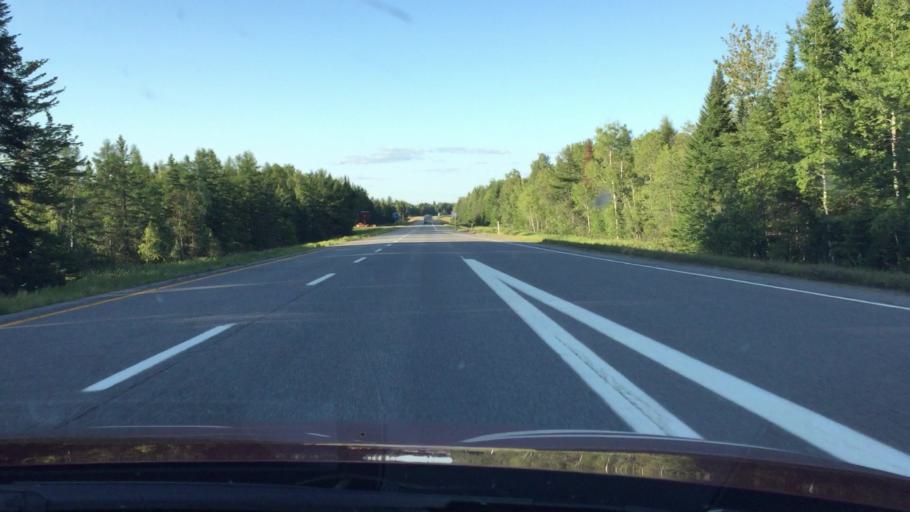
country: US
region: Maine
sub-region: Penobscot County
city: Patten
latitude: 45.8768
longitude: -68.4105
